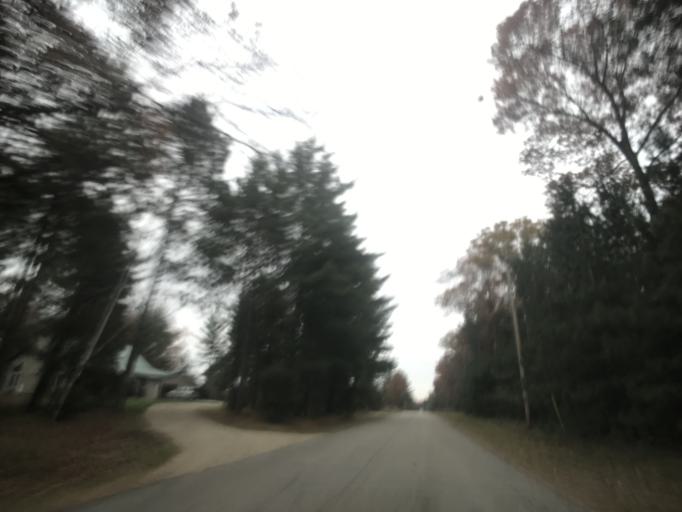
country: US
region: Wisconsin
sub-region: Oconto County
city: Gillett
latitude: 45.3085
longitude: -88.2706
